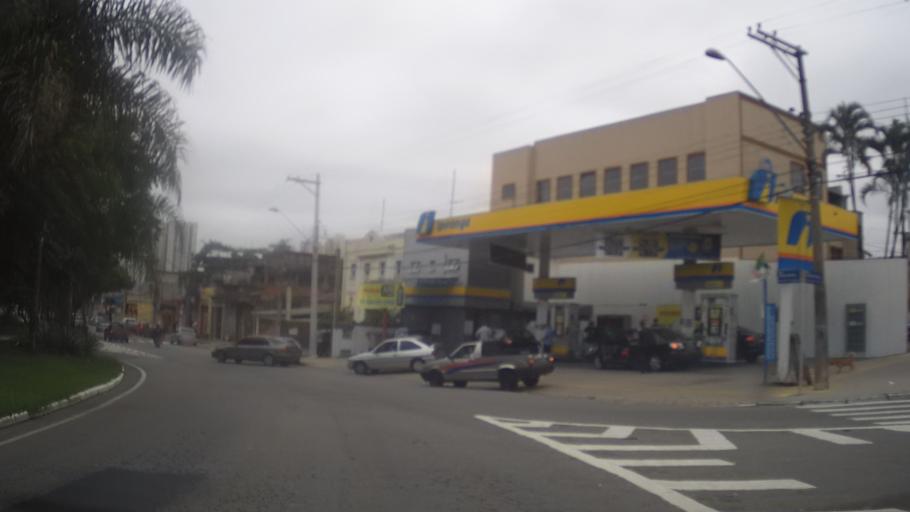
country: BR
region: Sao Paulo
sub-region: Guarulhos
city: Guarulhos
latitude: -23.4359
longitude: -46.5501
